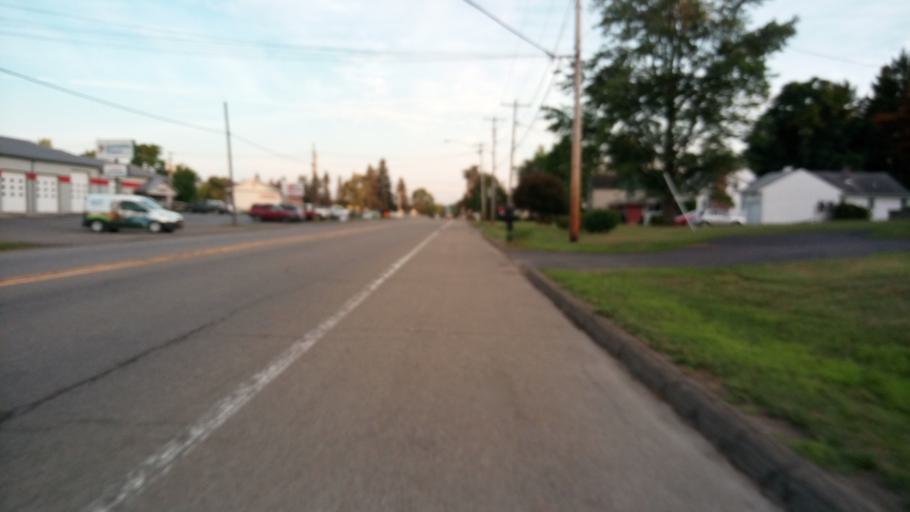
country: US
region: New York
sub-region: Chemung County
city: Horseheads
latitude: 42.1499
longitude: -76.8211
